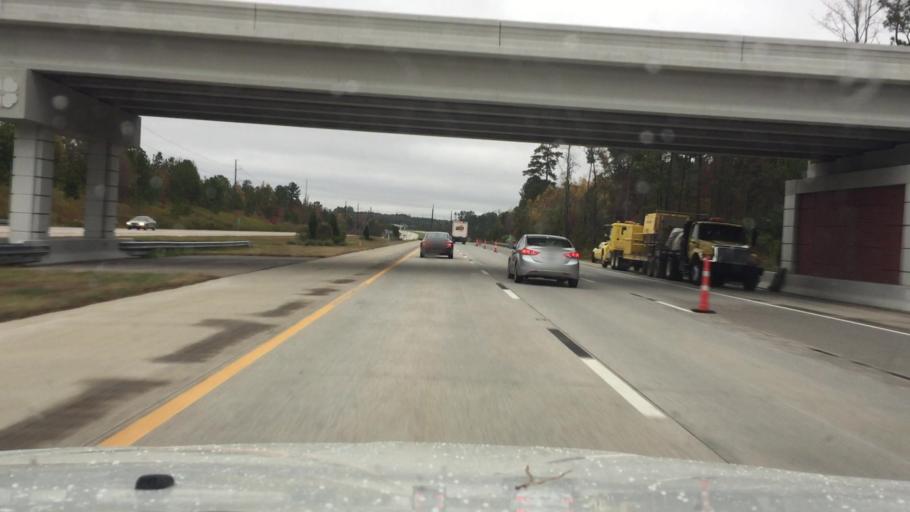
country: US
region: North Carolina
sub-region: Wake County
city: Green Level
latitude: 35.8089
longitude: -78.8921
